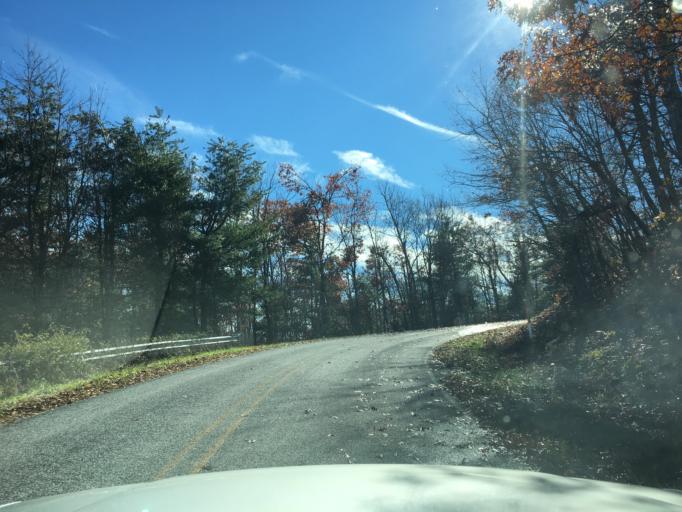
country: US
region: North Carolina
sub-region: Henderson County
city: Valley Hill
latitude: 35.2335
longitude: -82.5322
